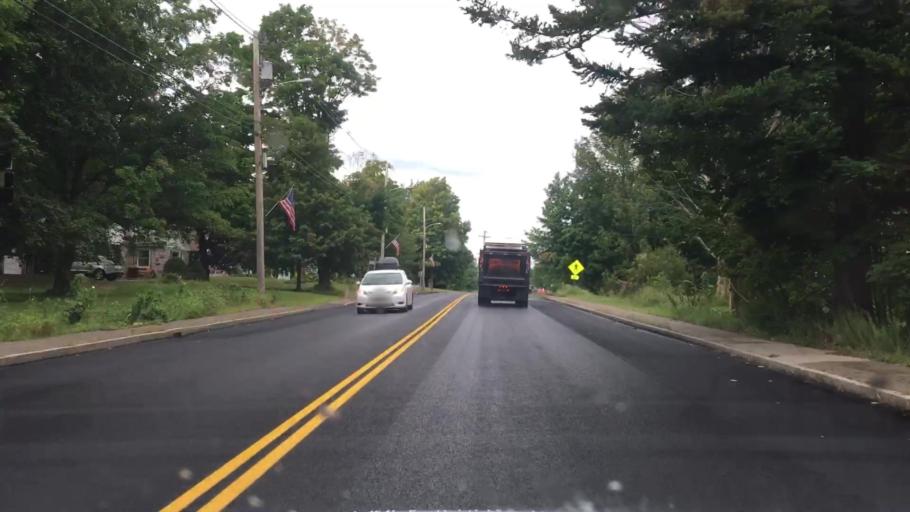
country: US
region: Maine
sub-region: York County
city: North Berwick
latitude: 43.3076
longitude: -70.7388
